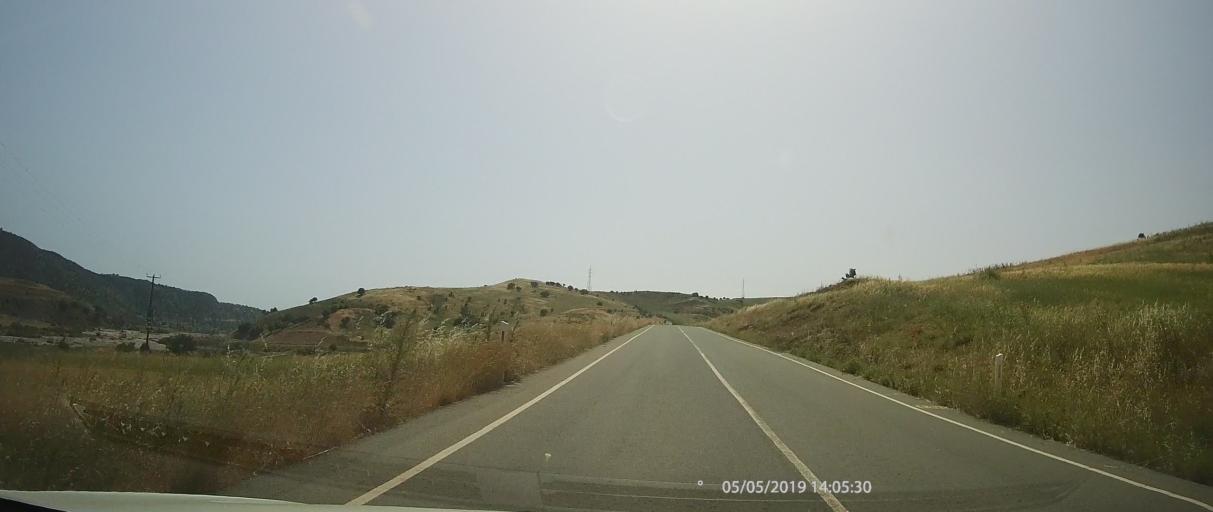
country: CY
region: Limassol
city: Pissouri
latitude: 34.7528
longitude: 32.6128
